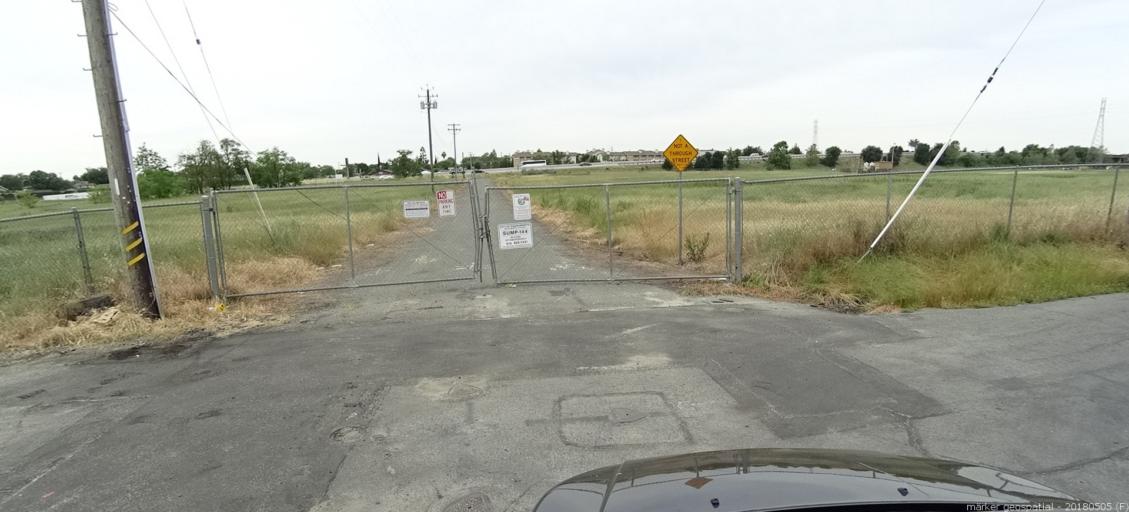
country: US
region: California
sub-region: Sacramento County
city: Rio Linda
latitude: 38.6439
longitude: -121.4431
